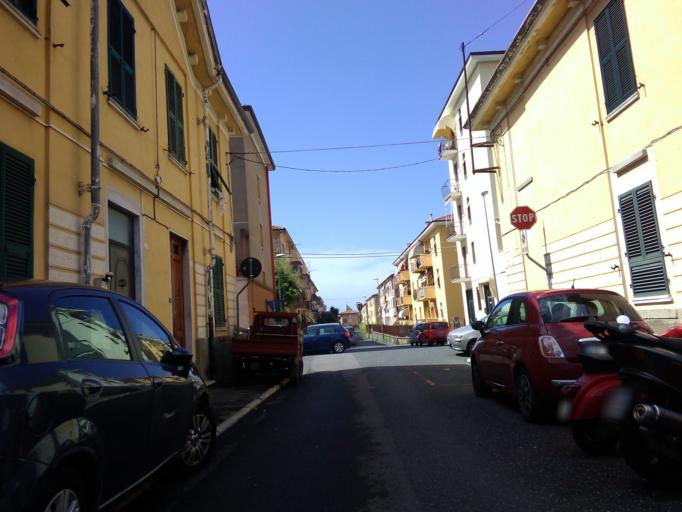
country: IT
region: Tuscany
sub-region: Provincia di Massa-Carrara
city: Carrara
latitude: 44.0640
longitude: 10.0761
